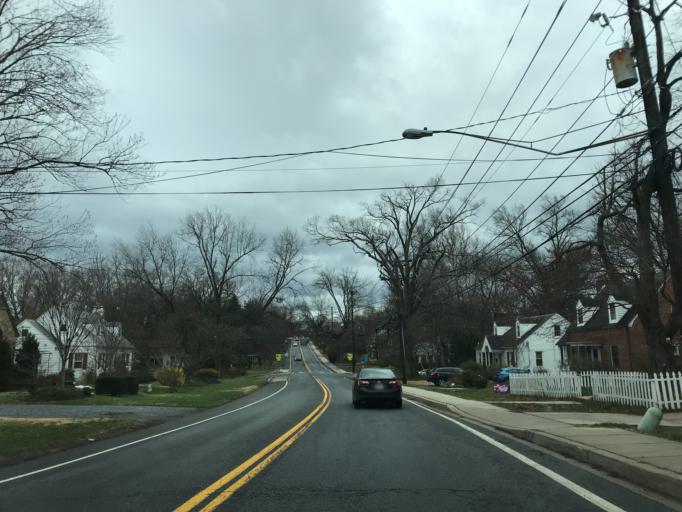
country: US
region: Maryland
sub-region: Montgomery County
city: Four Corners
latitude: 39.0077
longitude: -77.0081
